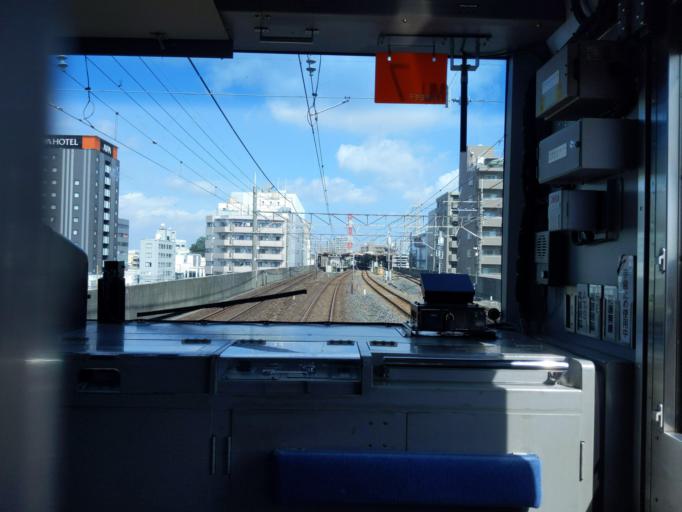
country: JP
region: Chiba
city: Funabashi
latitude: 35.7049
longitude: 139.9580
